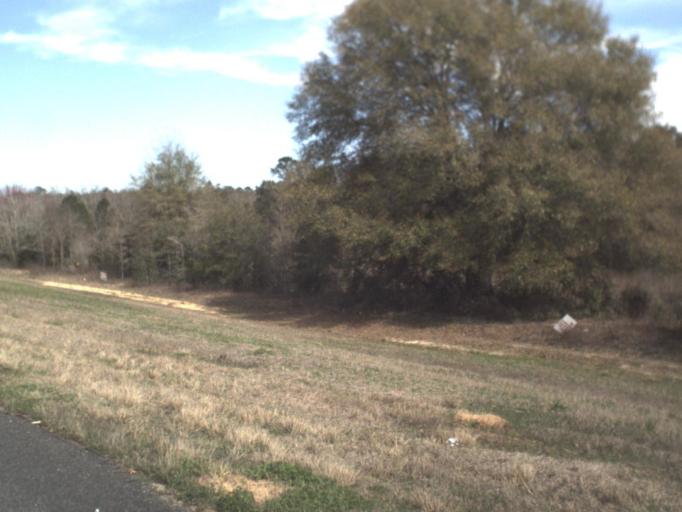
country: US
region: Florida
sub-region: Bay County
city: Youngstown
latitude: 30.5741
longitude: -85.3869
